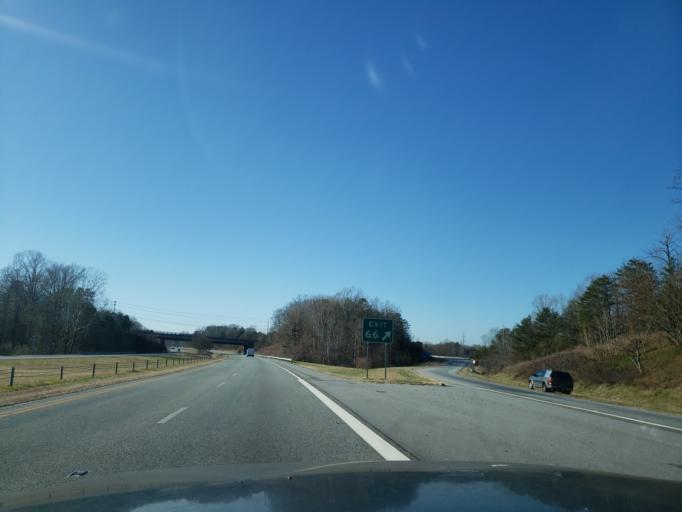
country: US
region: North Carolina
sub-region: Guilford County
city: High Point
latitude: 36.0090
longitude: -80.0067
